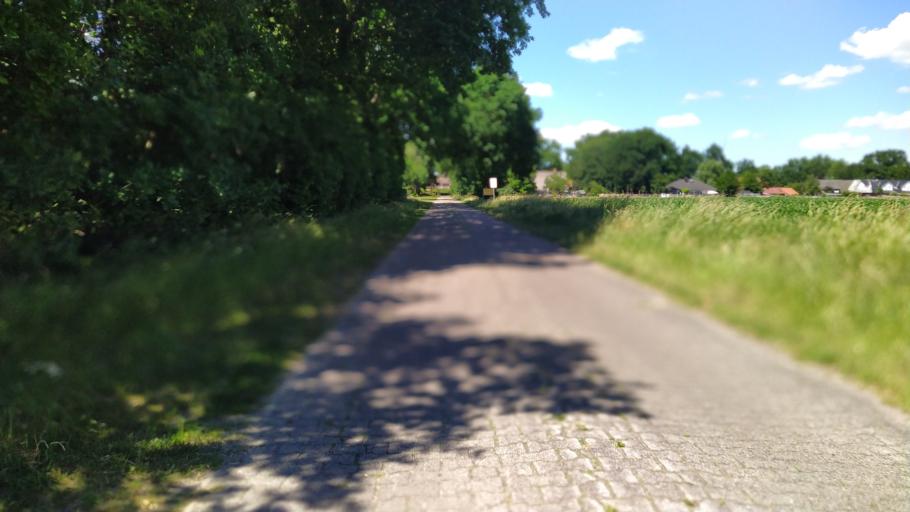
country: DE
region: Lower Saxony
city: Estorf
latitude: 53.5690
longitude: 9.2052
